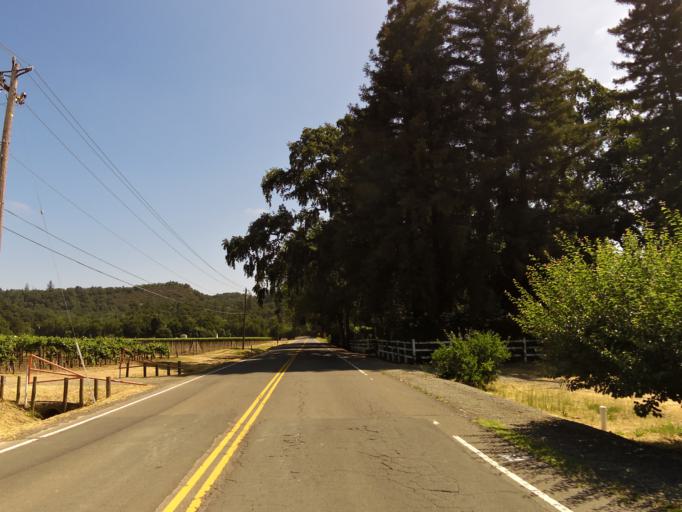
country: US
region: California
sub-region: Napa County
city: Saint Helena
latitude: 38.4928
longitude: -122.4288
